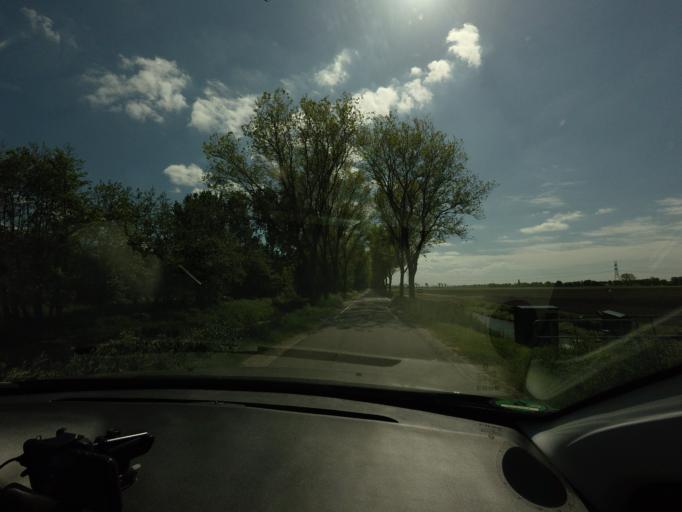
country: NL
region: North Holland
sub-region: Gemeente Beemster
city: Halfweg
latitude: 52.5658
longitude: 4.8743
